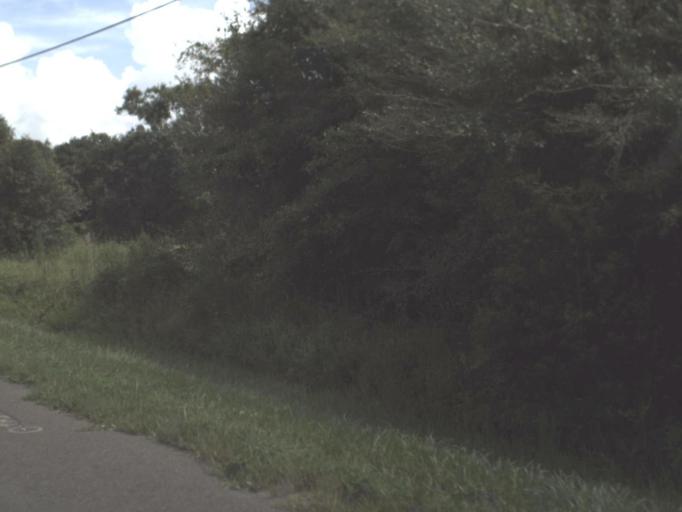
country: US
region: Florida
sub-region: DeSoto County
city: Southeast Arcadia
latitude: 27.1922
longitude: -81.8674
